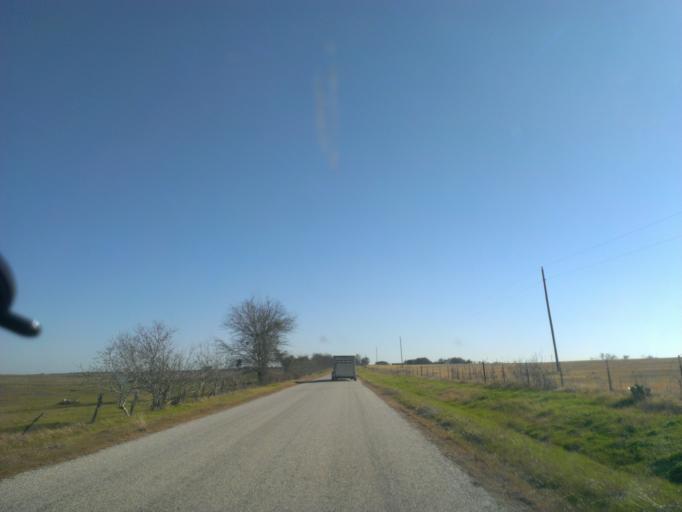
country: US
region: Texas
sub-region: Milam County
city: Thorndale
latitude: 30.5235
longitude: -97.2495
